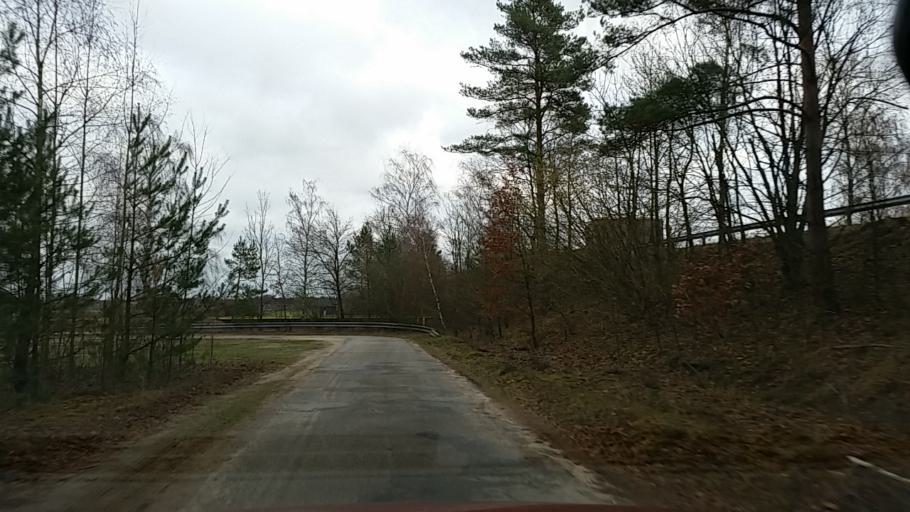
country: DE
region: Lower Saxony
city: Wieren
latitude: 52.8775
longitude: 10.6410
